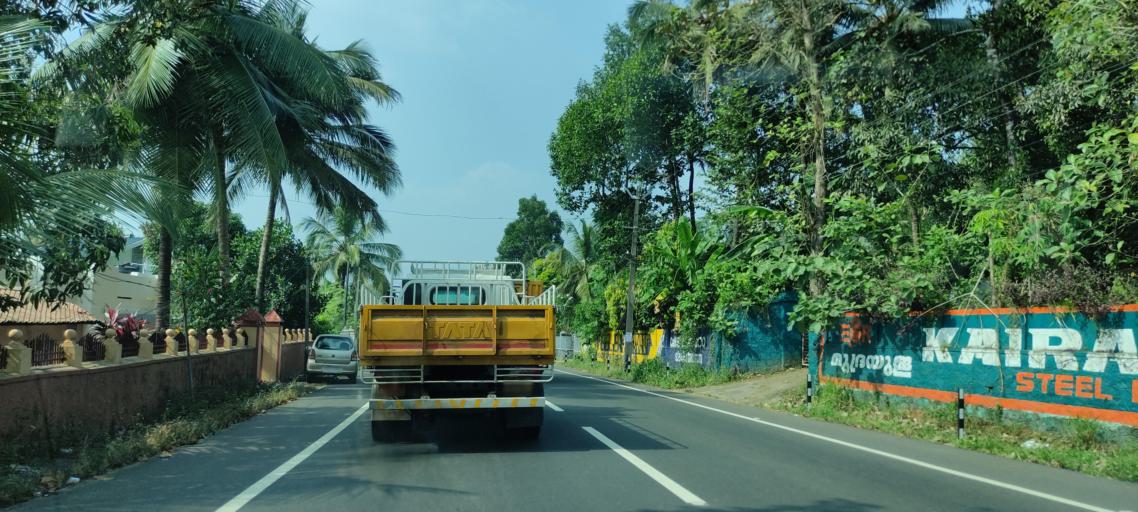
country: IN
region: Kerala
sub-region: Alappuzha
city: Chengannur
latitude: 9.2528
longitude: 76.6634
